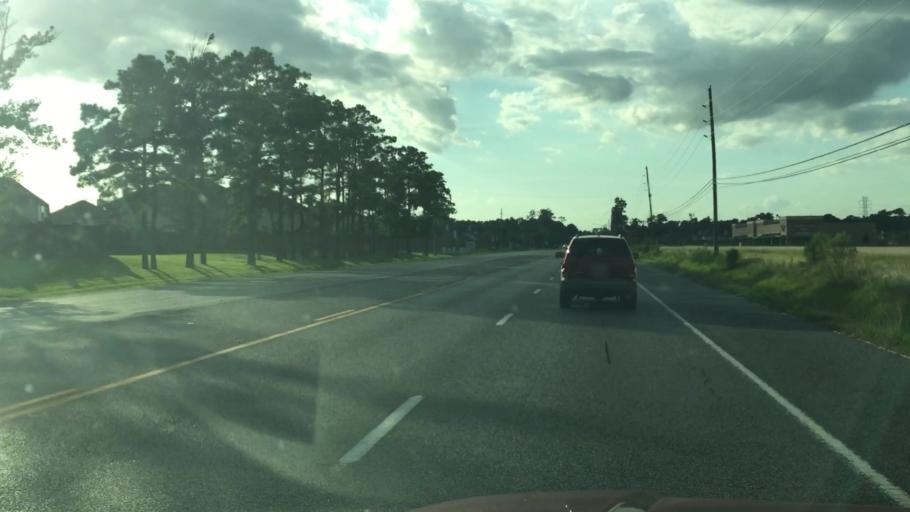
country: US
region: Texas
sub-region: Harris County
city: Tomball
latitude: 30.0769
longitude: -95.5586
